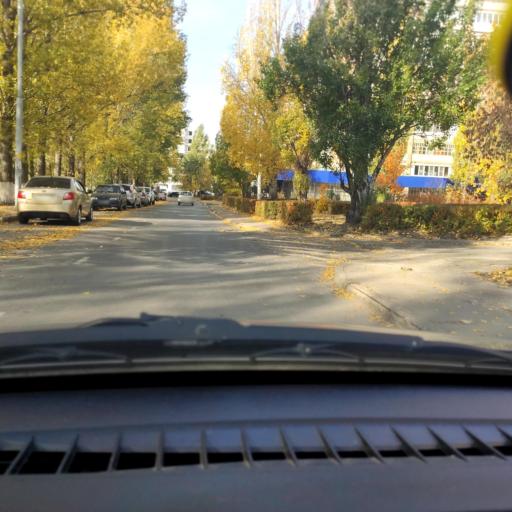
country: RU
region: Samara
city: Tol'yatti
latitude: 53.5337
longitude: 49.2911
